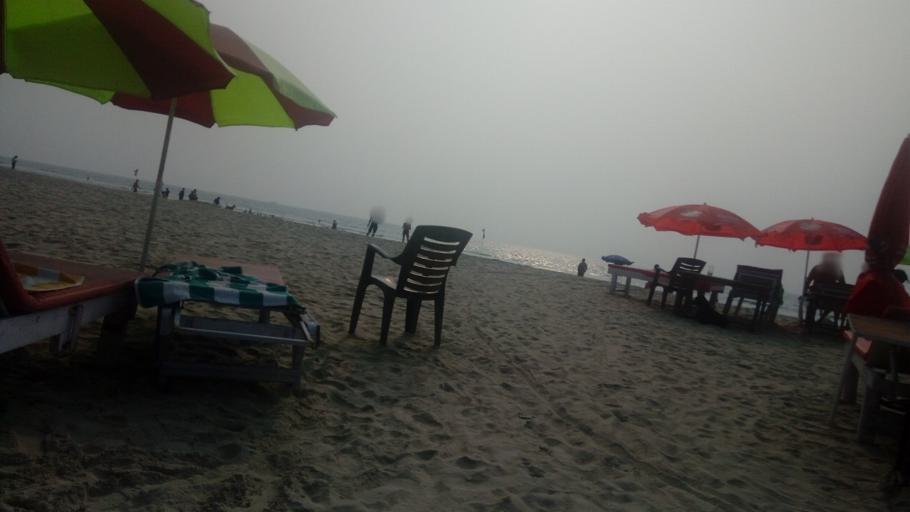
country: IN
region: Goa
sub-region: South Goa
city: Benaulim
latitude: 15.2575
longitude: 73.9189
